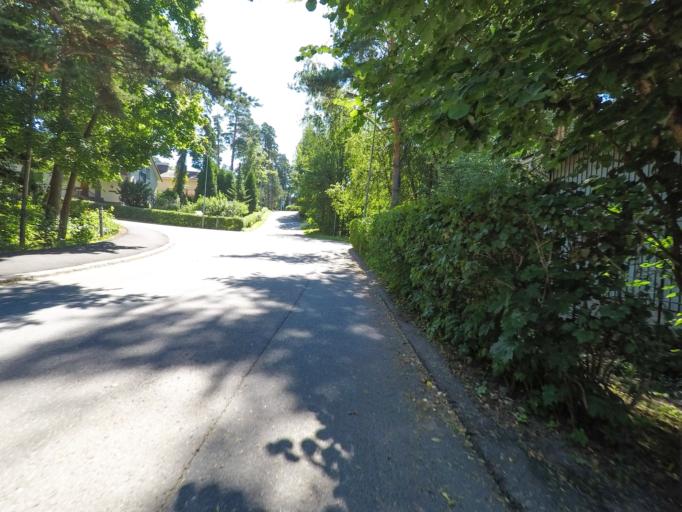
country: FI
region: Uusimaa
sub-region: Helsinki
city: Vantaa
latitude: 60.1903
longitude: 25.0655
